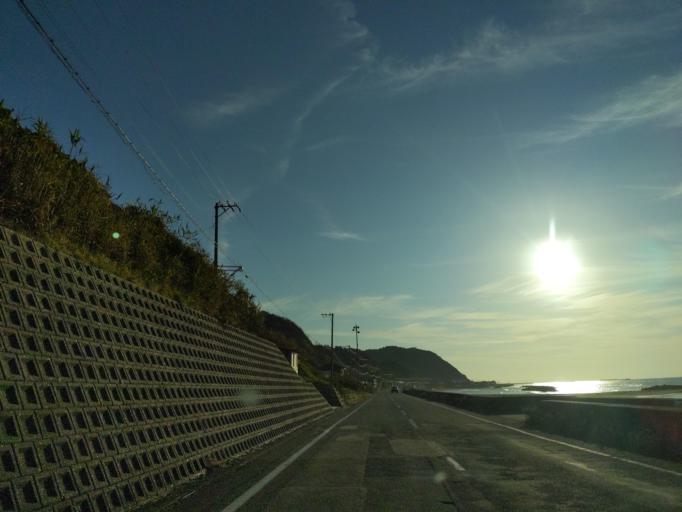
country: JP
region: Niigata
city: Nagaoka
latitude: 37.5581
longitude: 138.7131
